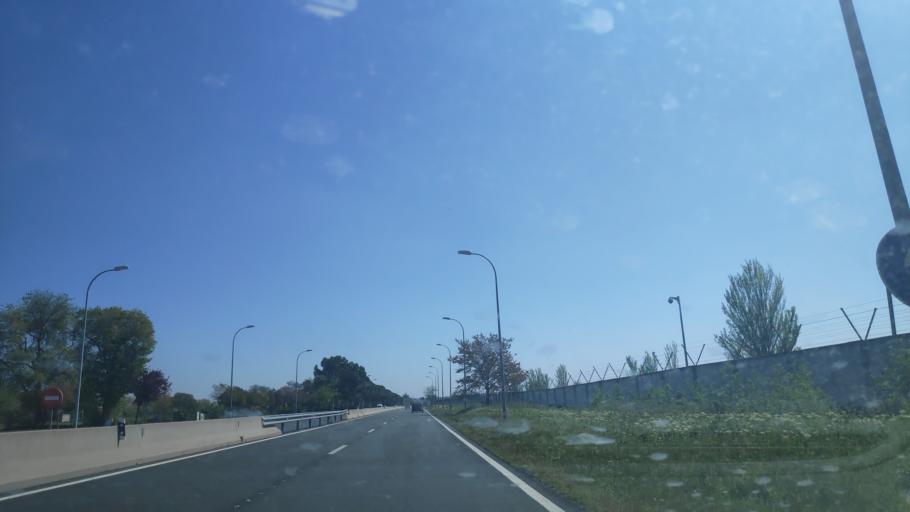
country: ES
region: Madrid
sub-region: Provincia de Madrid
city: Getafe
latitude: 40.3046
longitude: -3.7177
